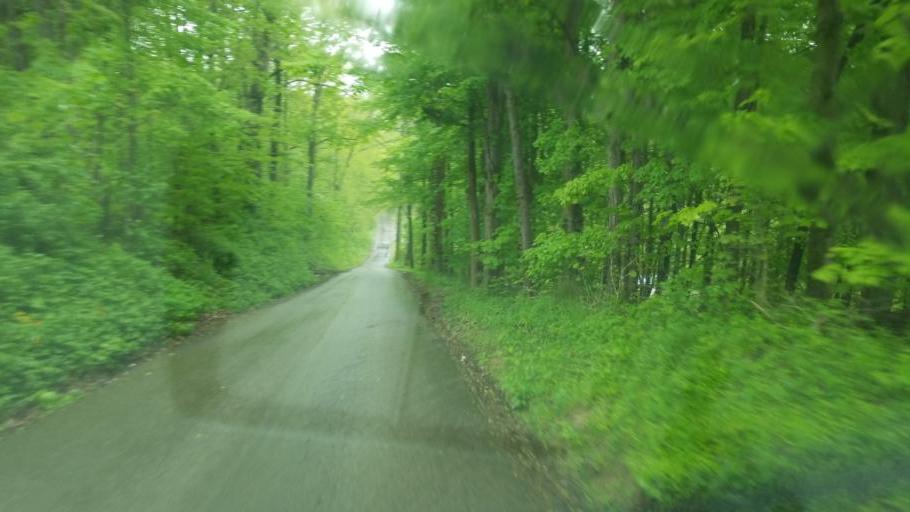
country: US
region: Ohio
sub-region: Muskingum County
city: Frazeysburg
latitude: 40.1473
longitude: -82.0983
